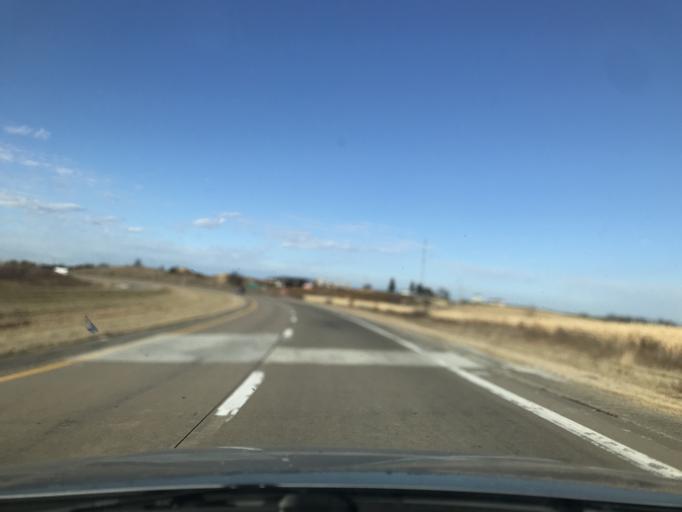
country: US
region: Iowa
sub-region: Jackson County
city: Maquoketa
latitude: 42.0410
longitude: -90.6552
